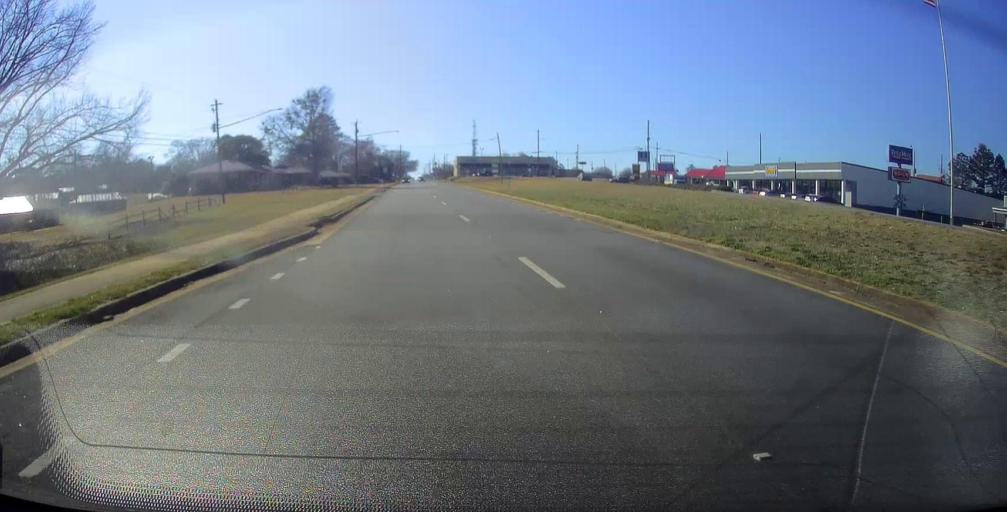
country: US
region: Georgia
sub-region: Sumter County
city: Americus
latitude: 32.0713
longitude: -84.2107
